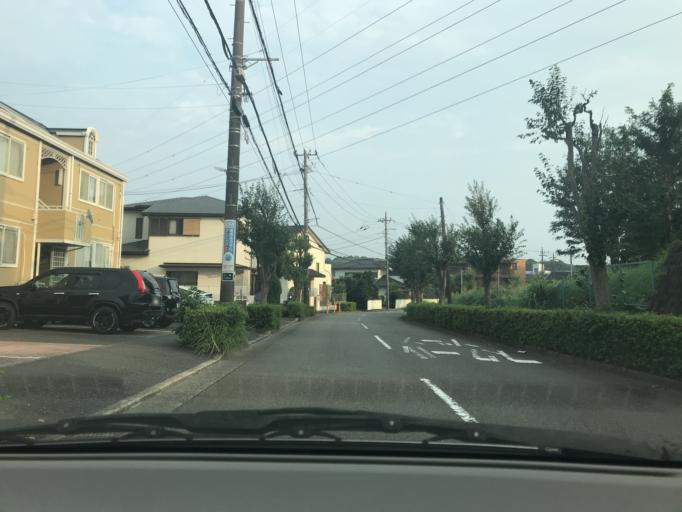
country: JP
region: Kanagawa
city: Fujisawa
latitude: 35.3677
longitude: 139.4498
